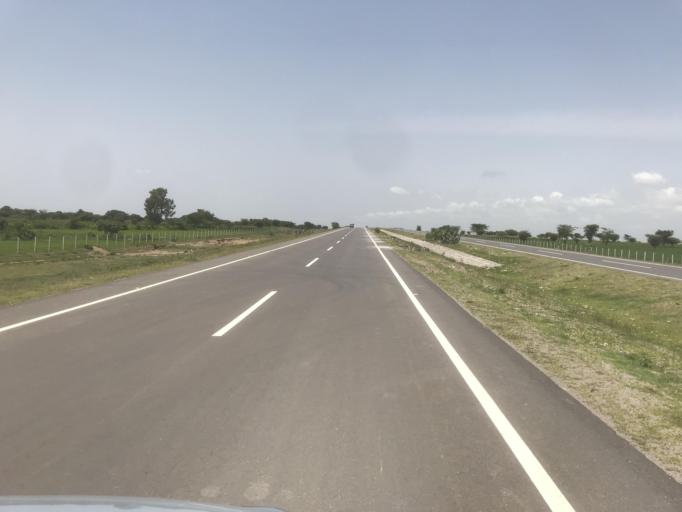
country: ET
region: Oromiya
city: Mojo
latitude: 8.2711
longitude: 38.9082
